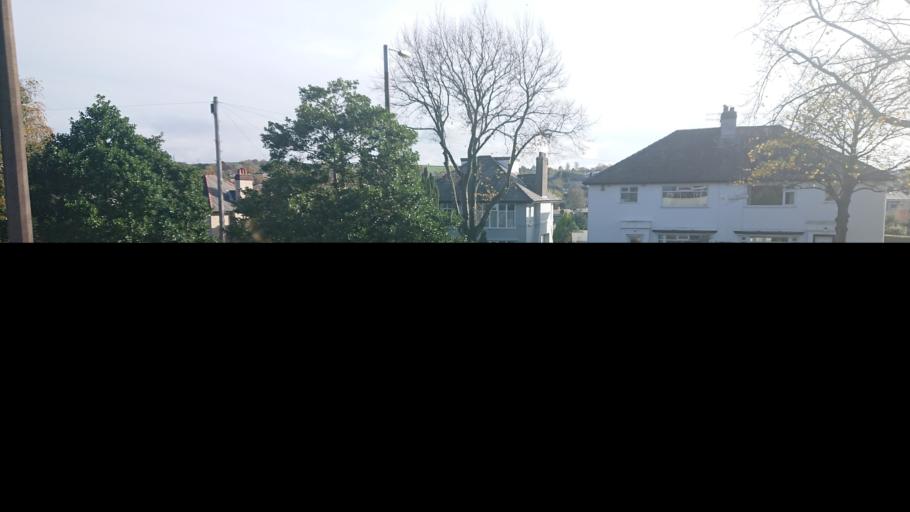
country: GB
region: England
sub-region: Lancashire
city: Lancaster
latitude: 54.0297
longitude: -2.7948
